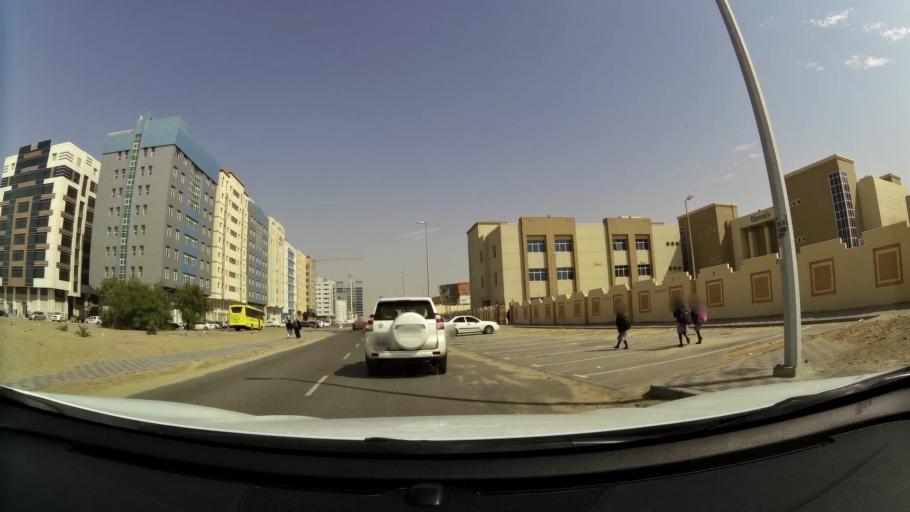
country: AE
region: Abu Dhabi
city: Abu Dhabi
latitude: 24.3398
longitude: 54.5303
